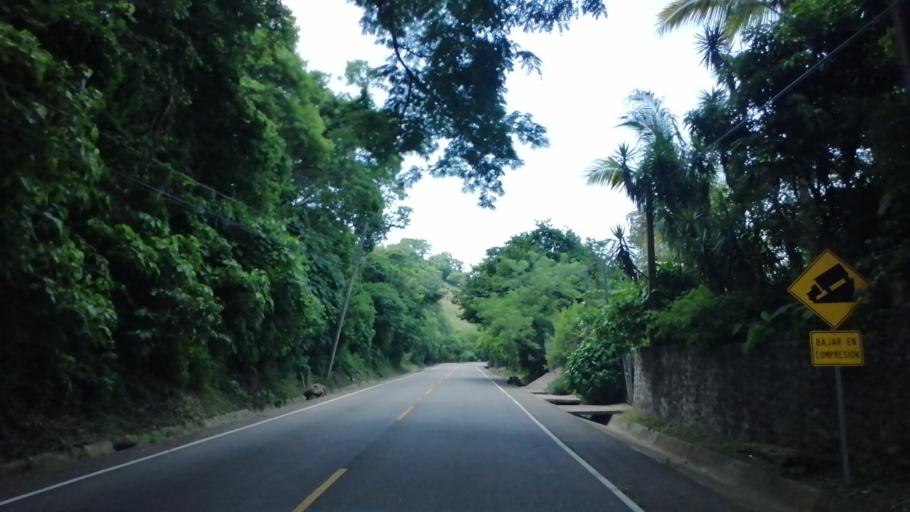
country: SV
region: Chalatenango
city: Nueva Concepcion
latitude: 14.1823
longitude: -89.3247
